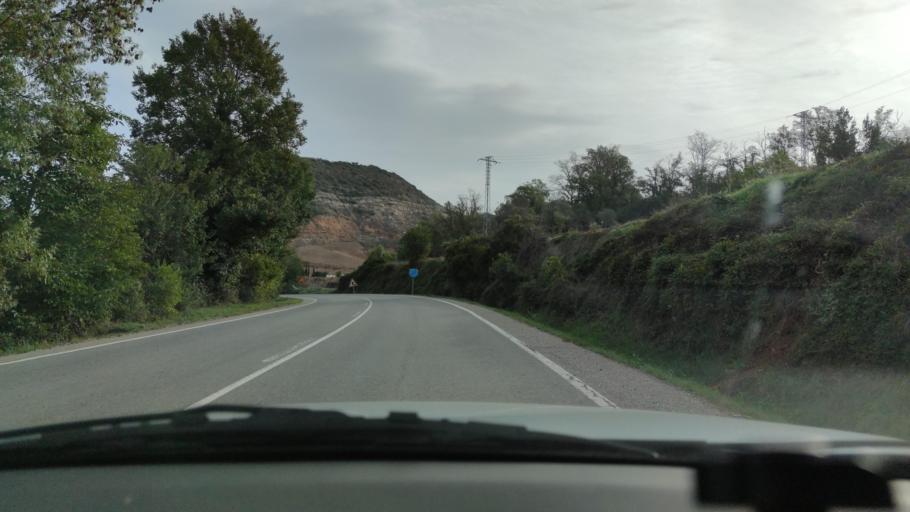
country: ES
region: Catalonia
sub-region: Provincia de Lleida
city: Artesa de Segre
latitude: 41.8963
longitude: 1.0568
